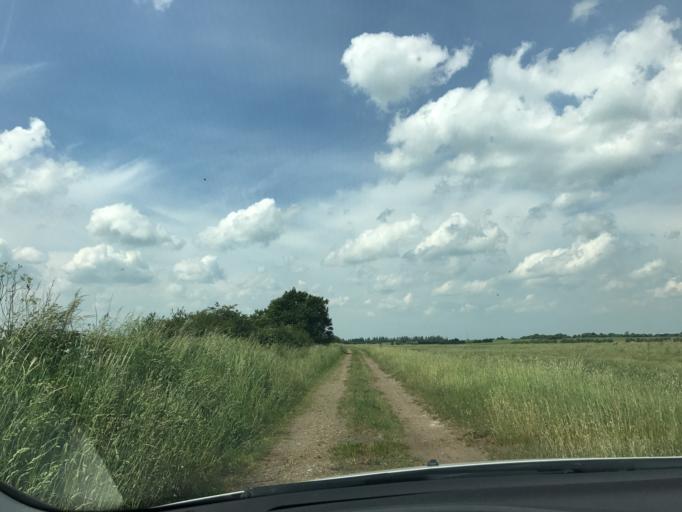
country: DE
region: Schleswig-Holstein
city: Ellhoft
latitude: 54.9244
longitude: 8.9481
